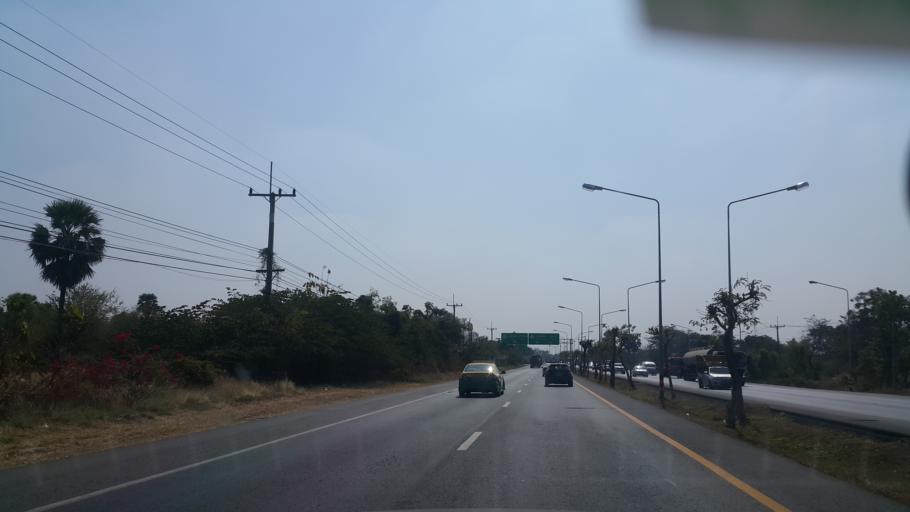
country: TH
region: Nakhon Ratchasima
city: Non Daeng
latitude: 15.3518
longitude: 102.4477
